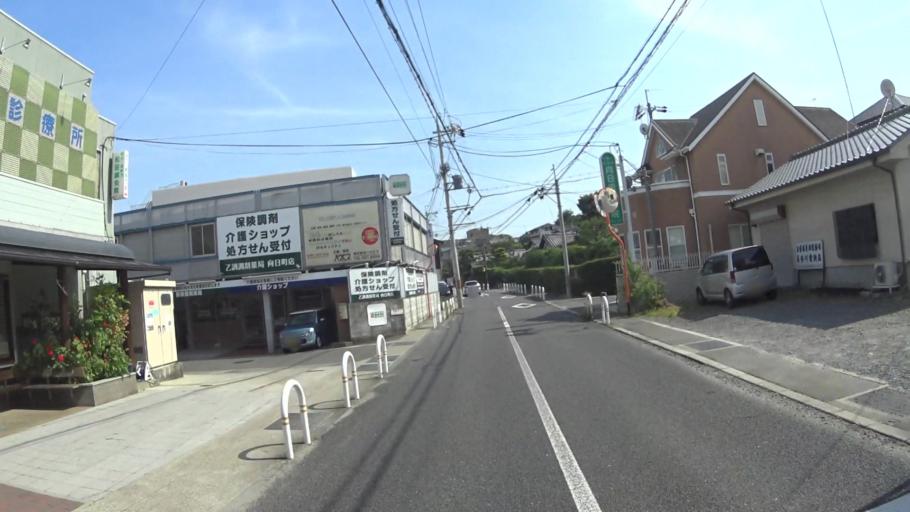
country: JP
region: Kyoto
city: Muko
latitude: 34.9507
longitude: 135.7001
